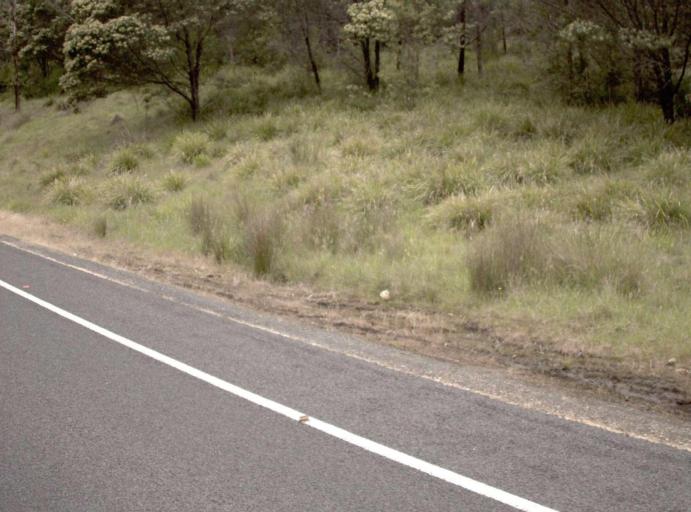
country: AU
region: New South Wales
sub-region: Bombala
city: Bombala
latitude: -37.2307
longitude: 149.2749
